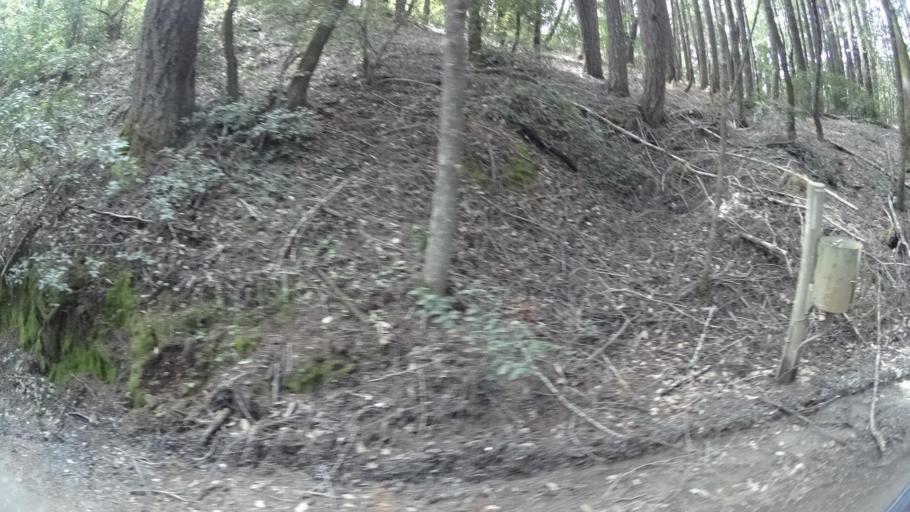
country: US
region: California
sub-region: Humboldt County
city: Redway
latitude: 40.0274
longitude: -123.8423
